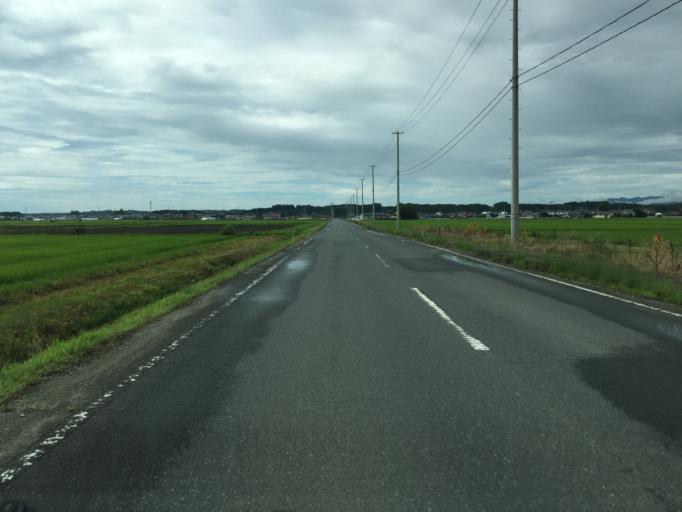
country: JP
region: Miyagi
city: Marumori
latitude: 37.7941
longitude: 140.9569
